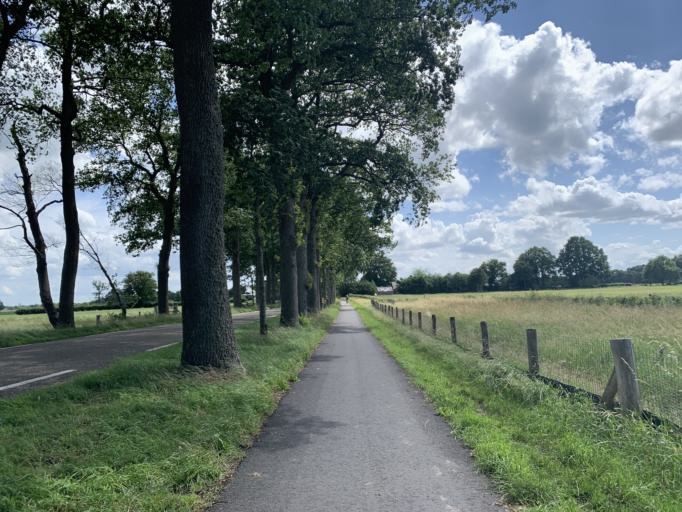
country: NL
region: Drenthe
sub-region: Gemeente Tynaarlo
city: Zuidlaren
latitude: 53.1307
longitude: 6.6596
